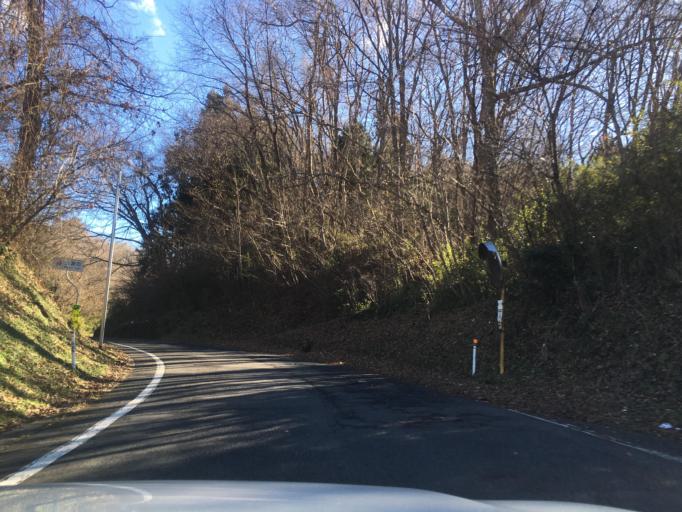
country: JP
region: Fukushima
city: Miharu
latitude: 37.4558
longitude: 140.4674
